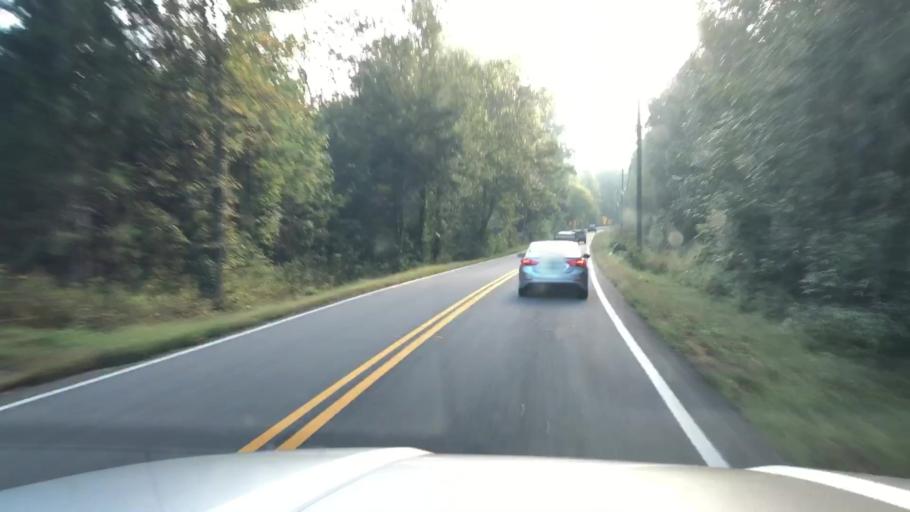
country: US
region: Georgia
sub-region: Bartow County
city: Emerson
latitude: 34.0813
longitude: -84.7629
